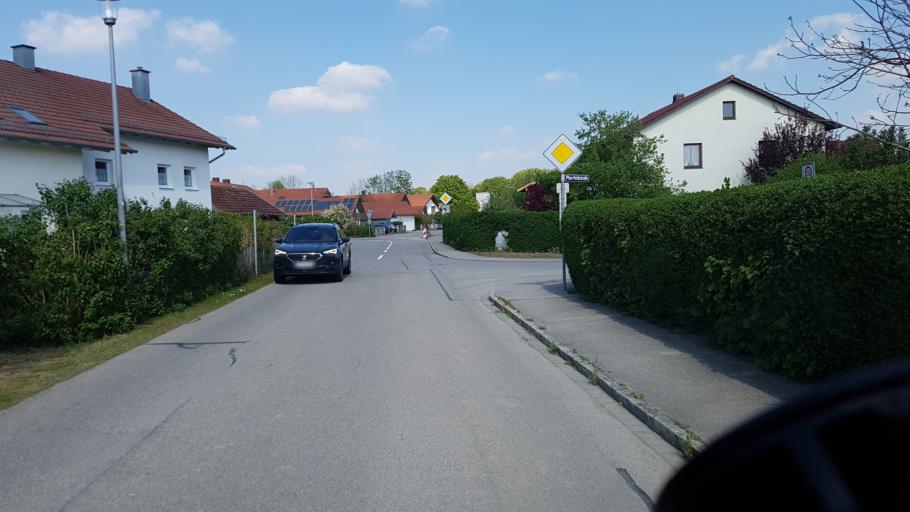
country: DE
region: Bavaria
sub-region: Upper Bavaria
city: Perach
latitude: 48.2431
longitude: 12.7466
